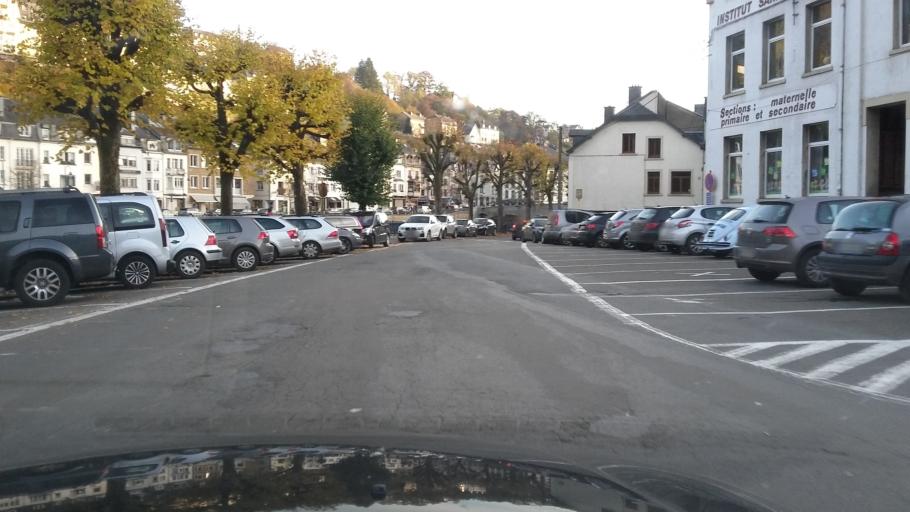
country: BE
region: Wallonia
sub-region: Province du Luxembourg
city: Bouillon
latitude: 49.7964
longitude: 5.0701
